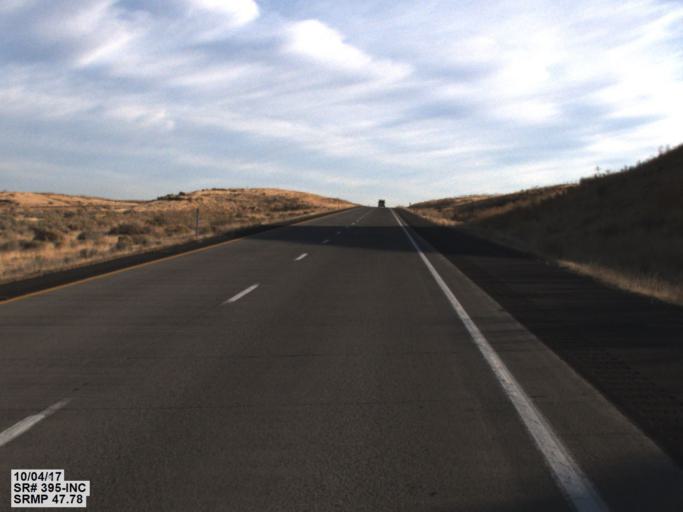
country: US
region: Washington
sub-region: Franklin County
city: Connell
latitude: 46.5864
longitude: -118.9650
